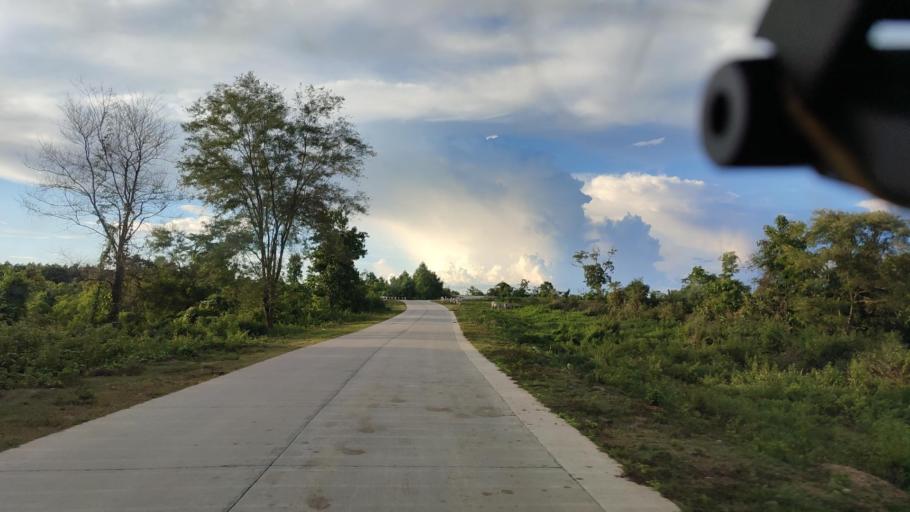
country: MM
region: Magway
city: Taungdwingyi
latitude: 20.0272
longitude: 95.7886
